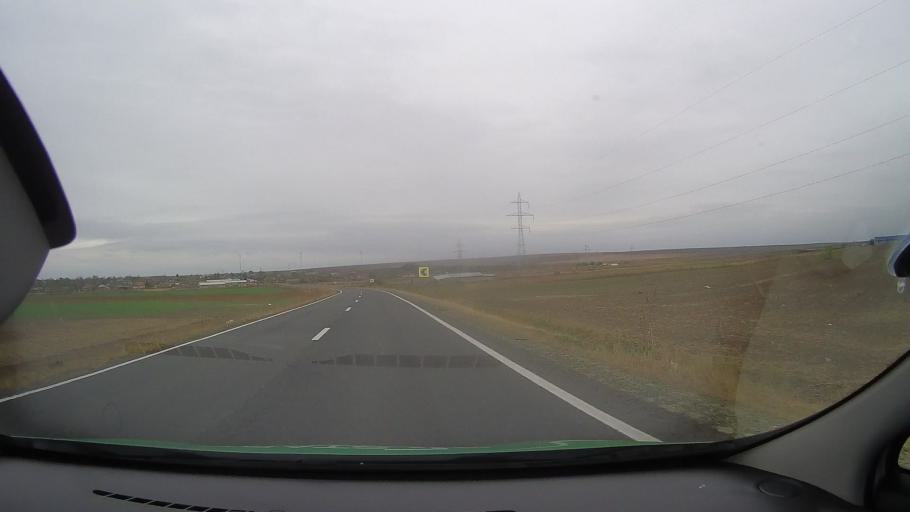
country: RO
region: Constanta
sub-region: Comuna Nicolae Balcescu
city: Dorobantu
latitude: 44.4156
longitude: 28.3161
